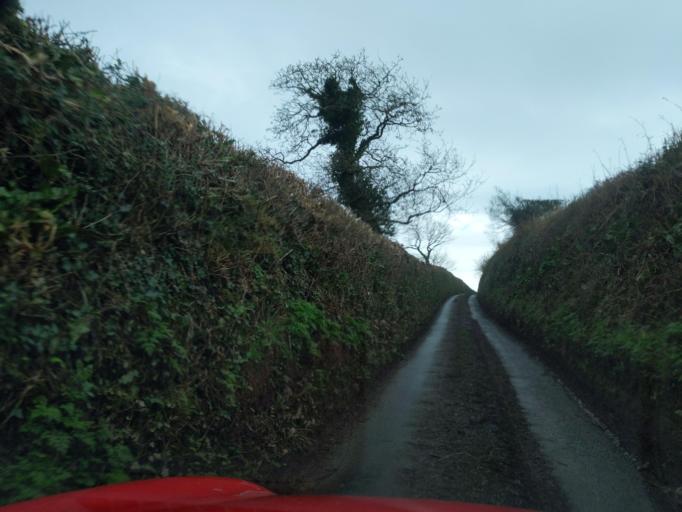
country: GB
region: England
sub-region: Devon
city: Salcombe
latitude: 50.2662
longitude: -3.6921
